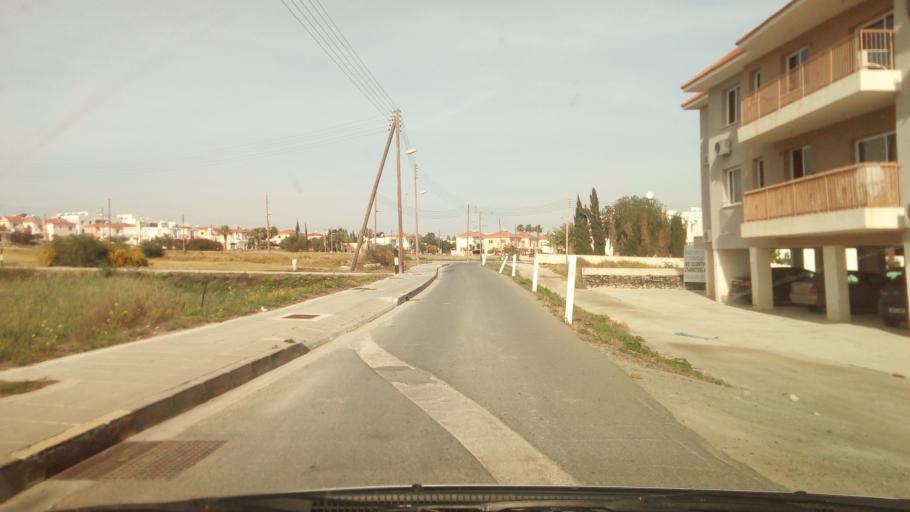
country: CY
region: Larnaka
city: Voroklini
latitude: 34.9767
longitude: 33.6513
